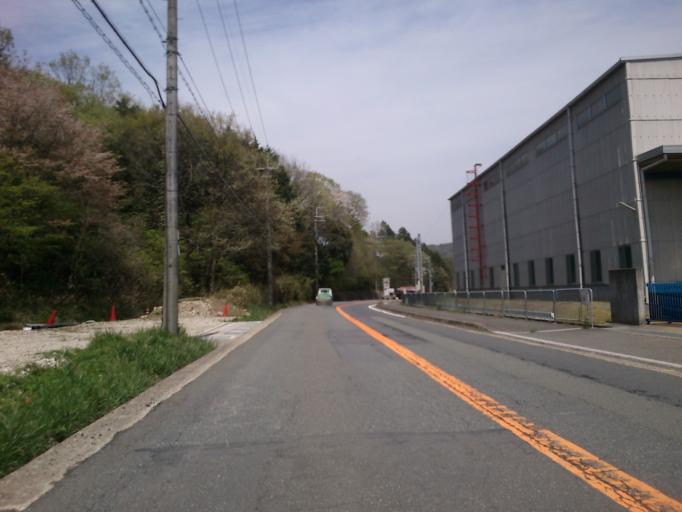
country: JP
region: Kyoto
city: Ayabe
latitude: 35.1697
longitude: 135.3601
